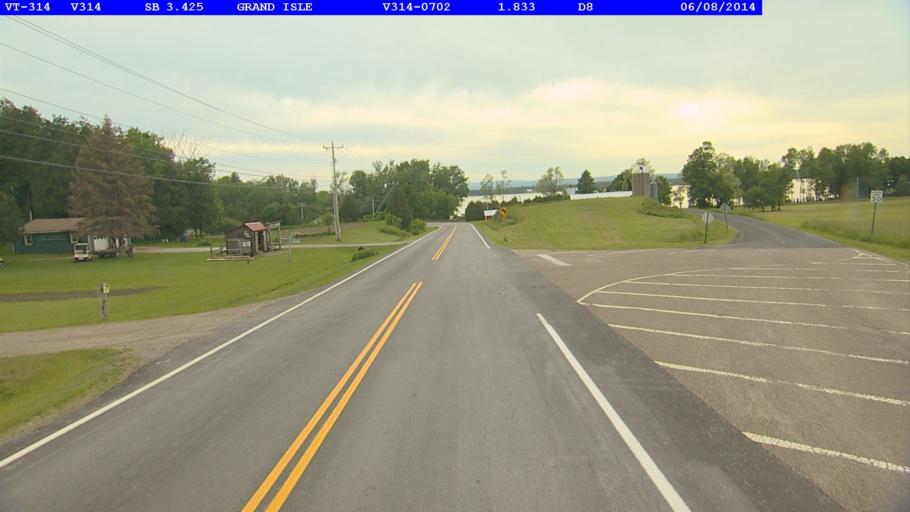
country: US
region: New York
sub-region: Clinton County
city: Cumberland Head
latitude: 44.7017
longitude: -73.3441
